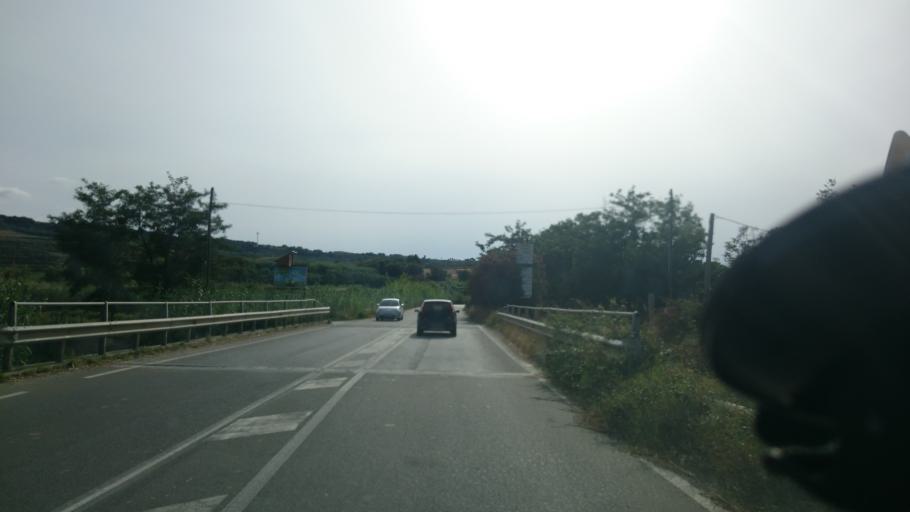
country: IT
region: Calabria
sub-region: Provincia di Vibo-Valentia
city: Pannaconi
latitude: 38.7094
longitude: 16.0707
